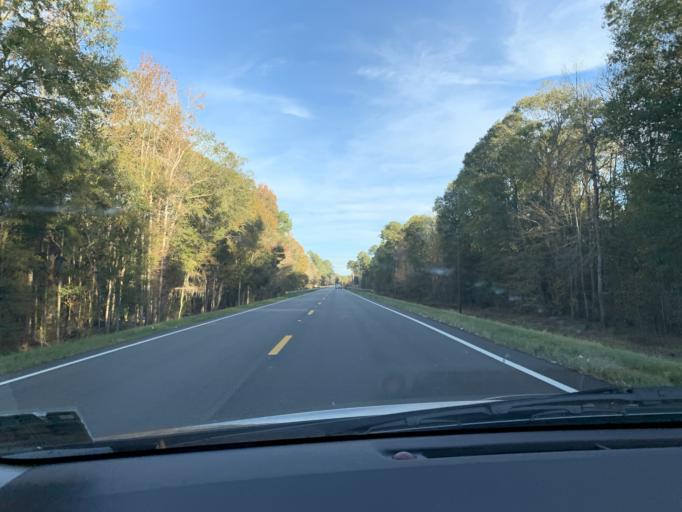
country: US
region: Georgia
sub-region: Irwin County
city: Ocilla
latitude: 31.5955
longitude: -83.1261
